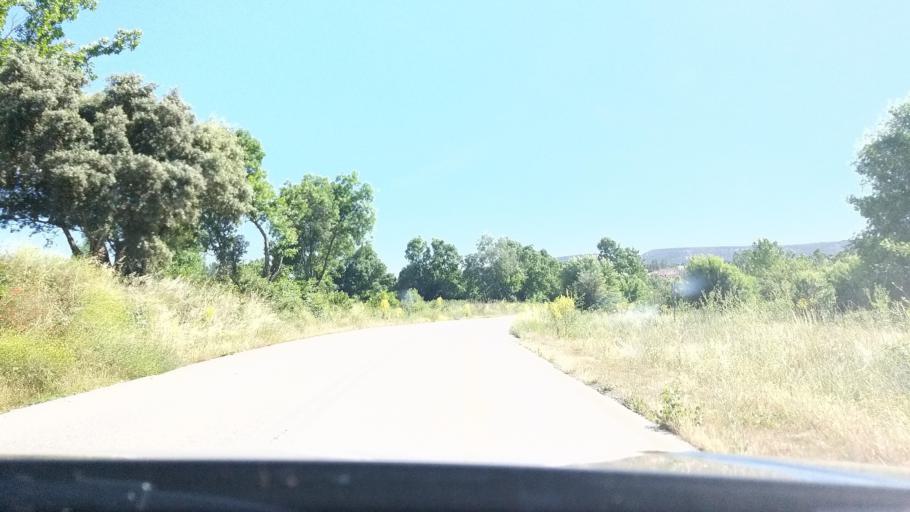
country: ES
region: Castille and Leon
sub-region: Provincia de Segovia
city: Pedraza
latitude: 41.1397
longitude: -3.8314
